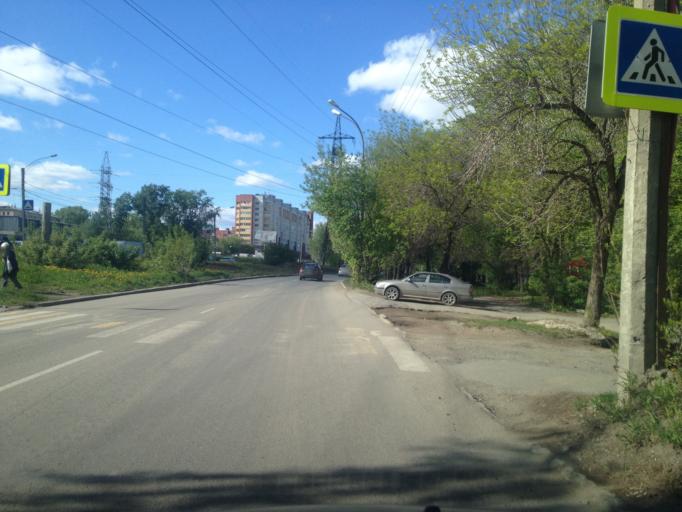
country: RU
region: Sverdlovsk
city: Sovkhoznyy
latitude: 56.7758
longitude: 60.5993
